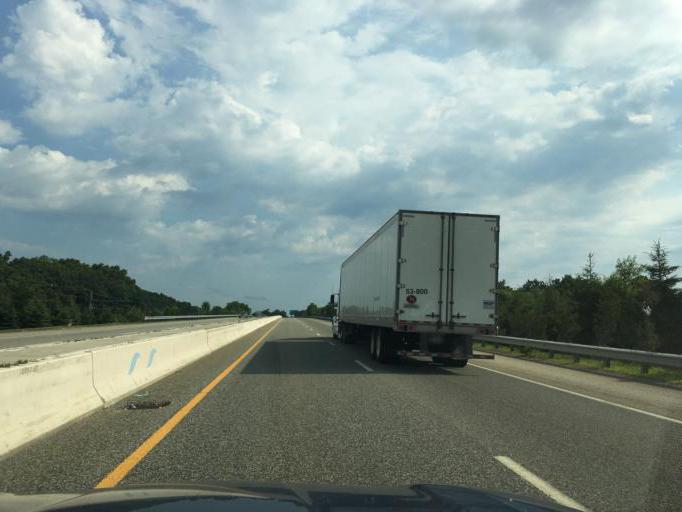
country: US
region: Rhode Island
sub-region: Kent County
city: East Greenwich
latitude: 41.6159
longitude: -71.4730
